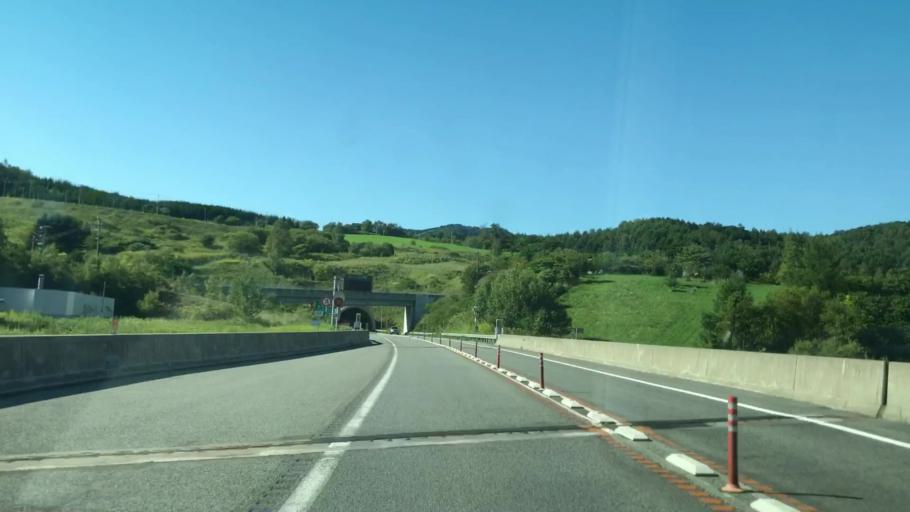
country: JP
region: Hokkaido
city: Date
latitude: 42.5506
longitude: 140.7900
